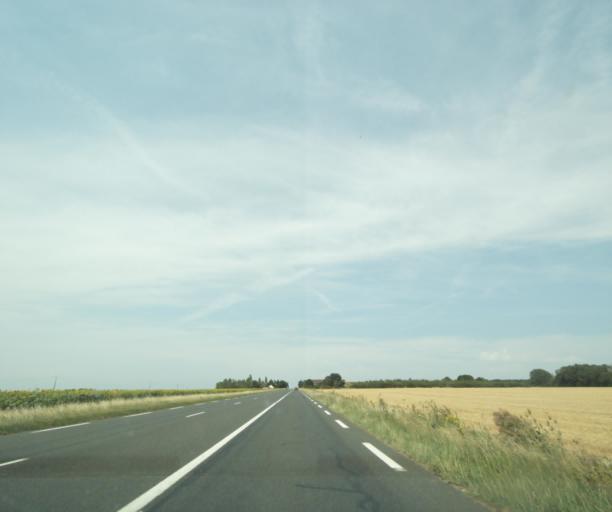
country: FR
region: Centre
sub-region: Departement d'Indre-et-Loire
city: Sainte-Maure-de-Touraine
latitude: 47.1685
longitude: 0.6525
